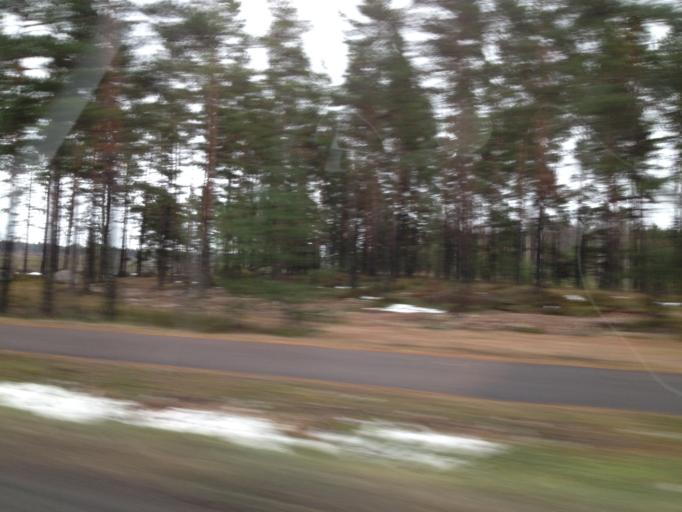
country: FI
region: Uusimaa
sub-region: Raaseporin
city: Hanko
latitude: 59.8438
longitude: 23.0076
